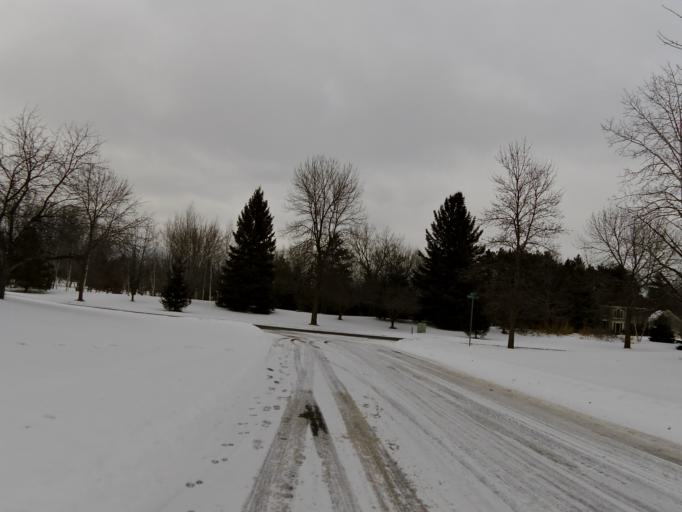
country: US
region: Minnesota
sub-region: Washington County
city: Lake Elmo
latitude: 44.9578
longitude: -92.8509
